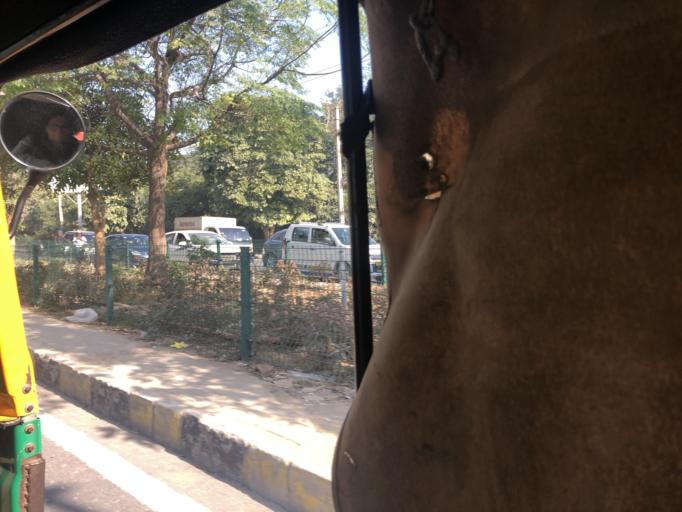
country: IN
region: Haryana
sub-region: Gurgaon
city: Gurgaon
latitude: 28.4301
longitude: 77.0913
